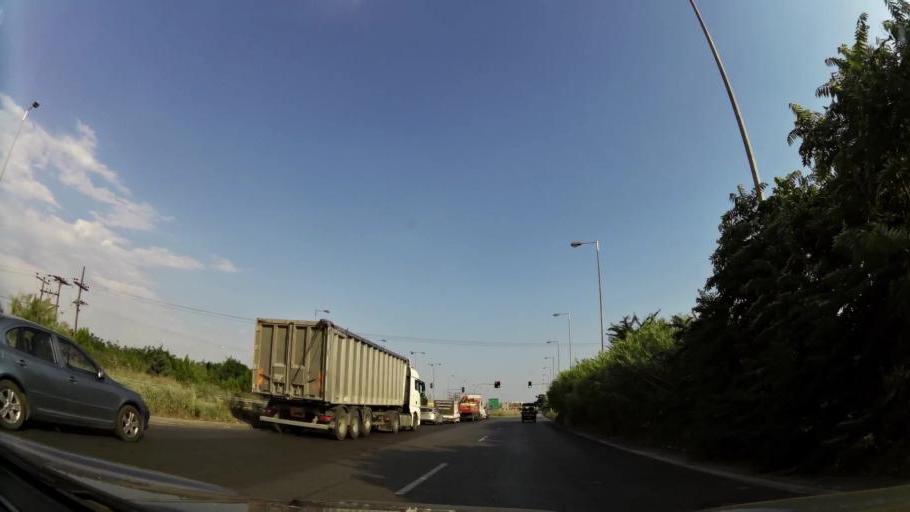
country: GR
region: Central Macedonia
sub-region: Nomos Thessalonikis
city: Nea Magnisia
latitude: 40.6934
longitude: 22.8464
